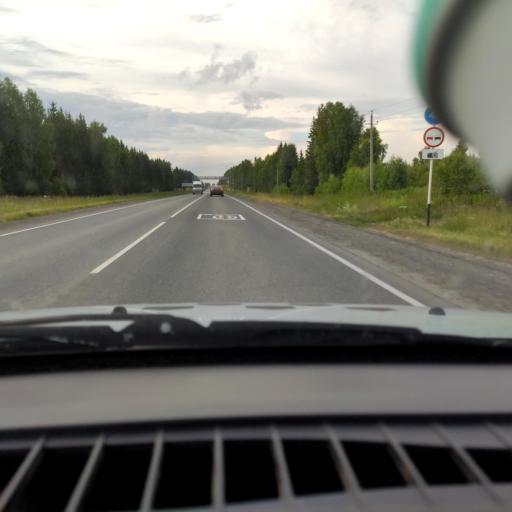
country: RU
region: Perm
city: Orda
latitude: 57.2570
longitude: 57.0067
